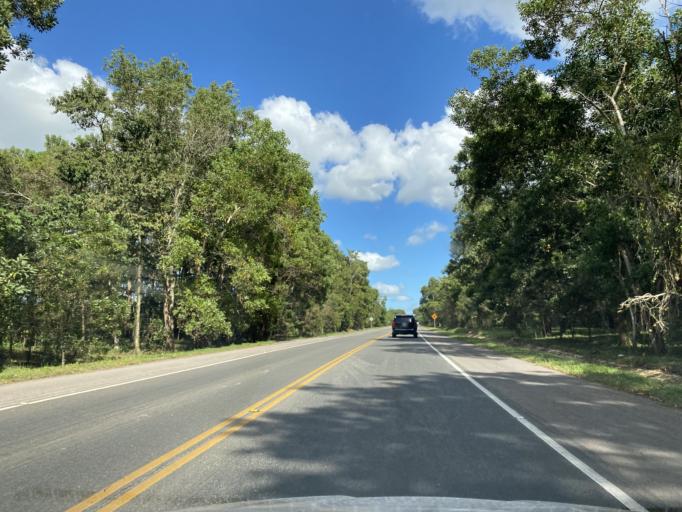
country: DO
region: Monte Plata
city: Monte Plata
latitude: 18.7620
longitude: -69.7622
